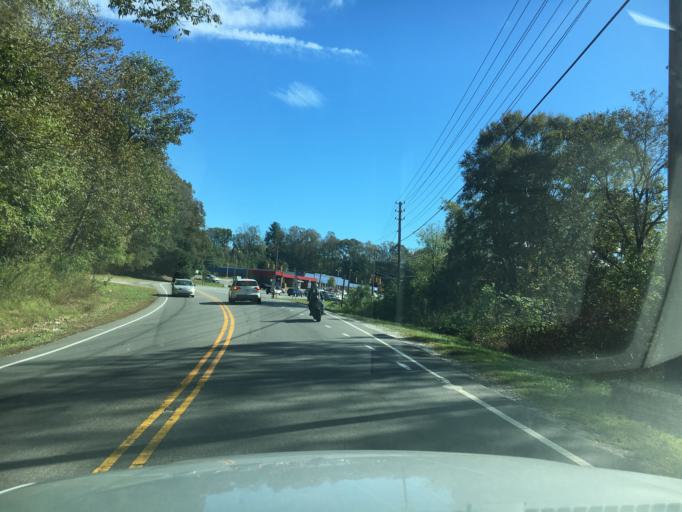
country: US
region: North Carolina
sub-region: Burke County
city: Morganton
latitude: 35.7508
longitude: -81.7053
